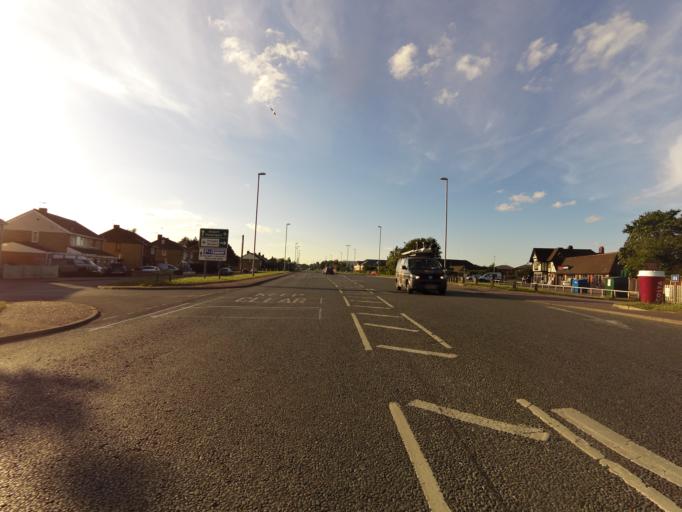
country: GB
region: England
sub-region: Norfolk
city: Norwich
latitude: 52.6658
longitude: 1.2726
